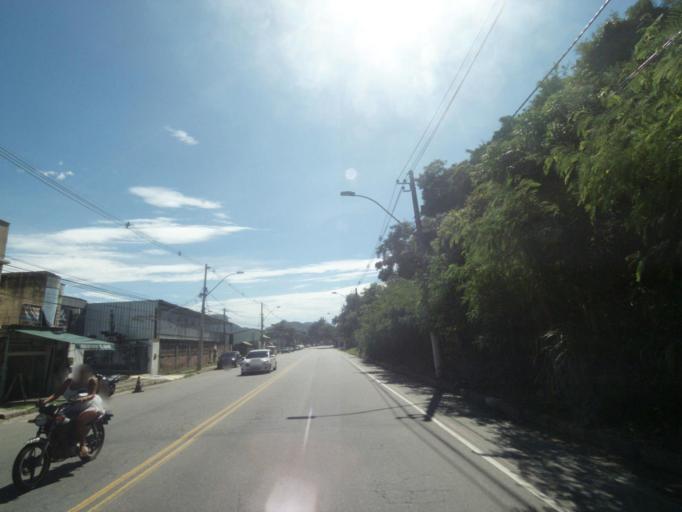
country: BR
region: Rio de Janeiro
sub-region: Niteroi
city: Niteroi
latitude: -22.9534
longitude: -43.0660
